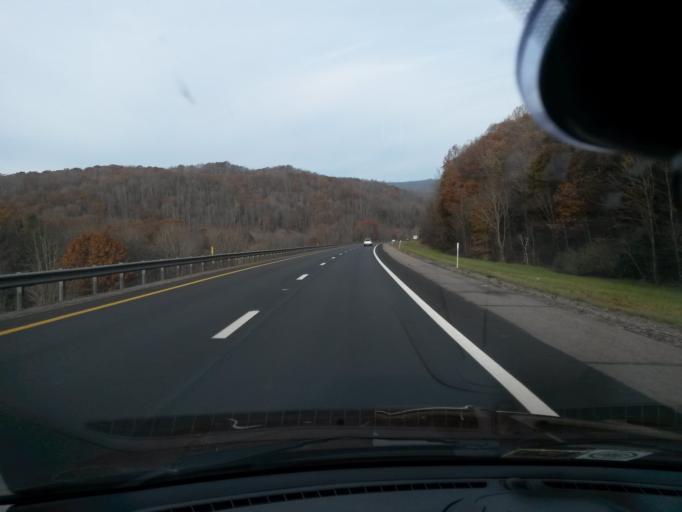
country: US
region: West Virginia
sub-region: Raleigh County
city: Prosperity
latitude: 37.8492
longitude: -81.2473
